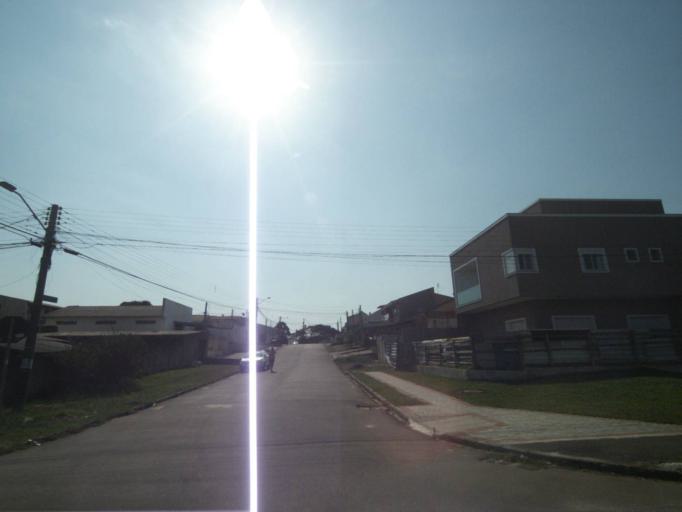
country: BR
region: Parana
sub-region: Curitiba
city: Curitiba
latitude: -25.4837
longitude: -49.3238
